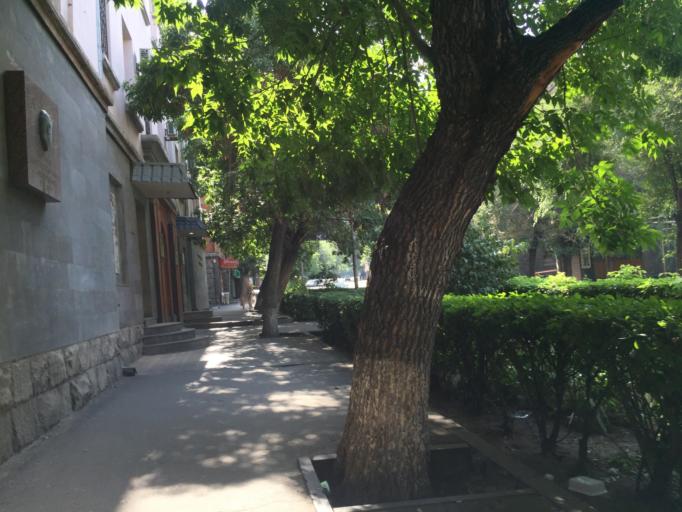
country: AM
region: Yerevan
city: Yerevan
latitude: 40.1892
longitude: 44.5164
